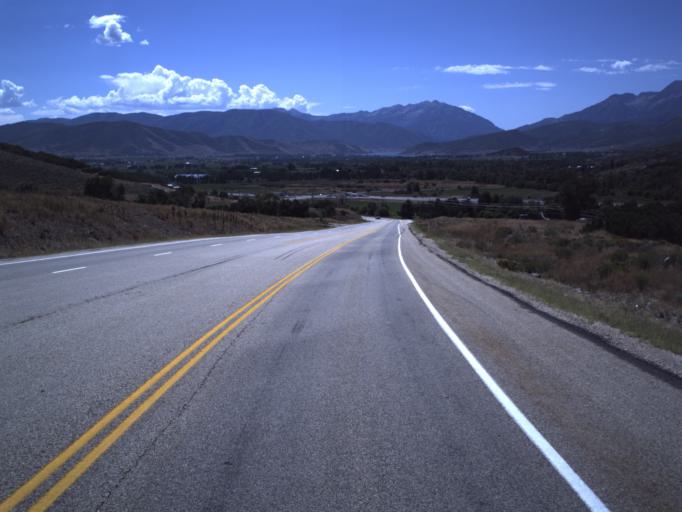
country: US
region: Utah
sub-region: Wasatch County
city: Heber
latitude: 40.5666
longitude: -111.4217
